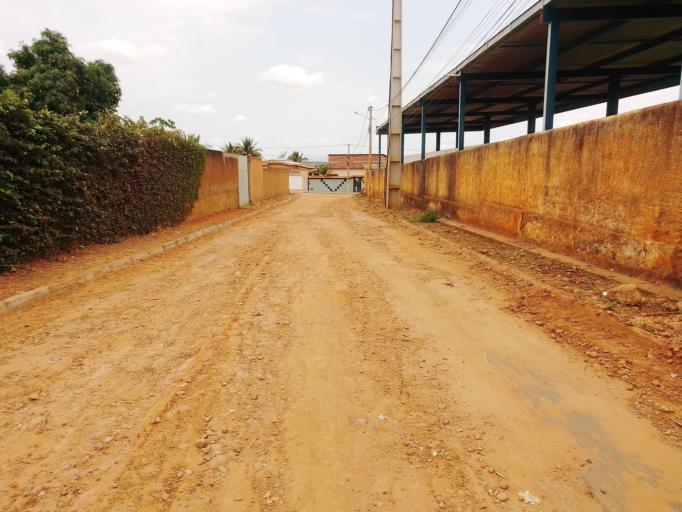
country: BR
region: Minas Gerais
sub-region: Sao Joao Do Paraiso
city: Sao Joao do Paraiso
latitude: -14.9004
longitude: -41.9714
